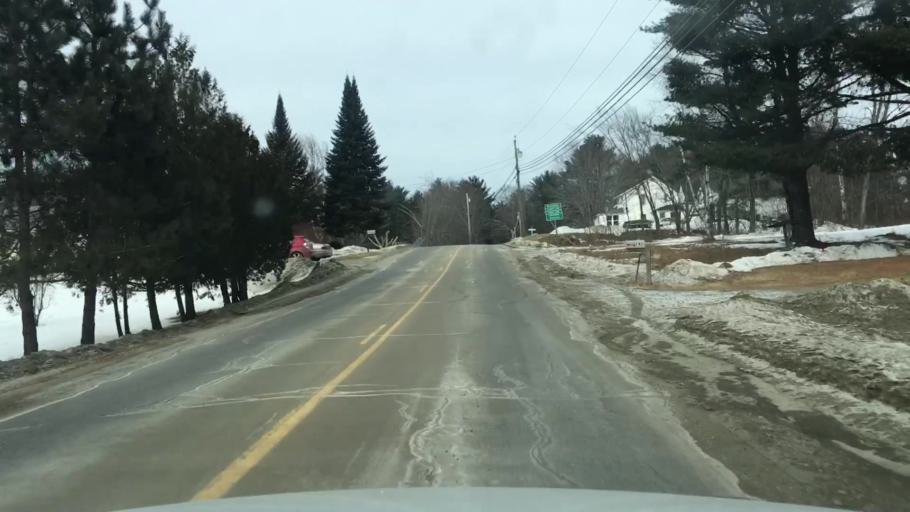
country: US
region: Maine
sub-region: Kennebec County
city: Chelsea
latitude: 44.2701
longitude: -69.6529
